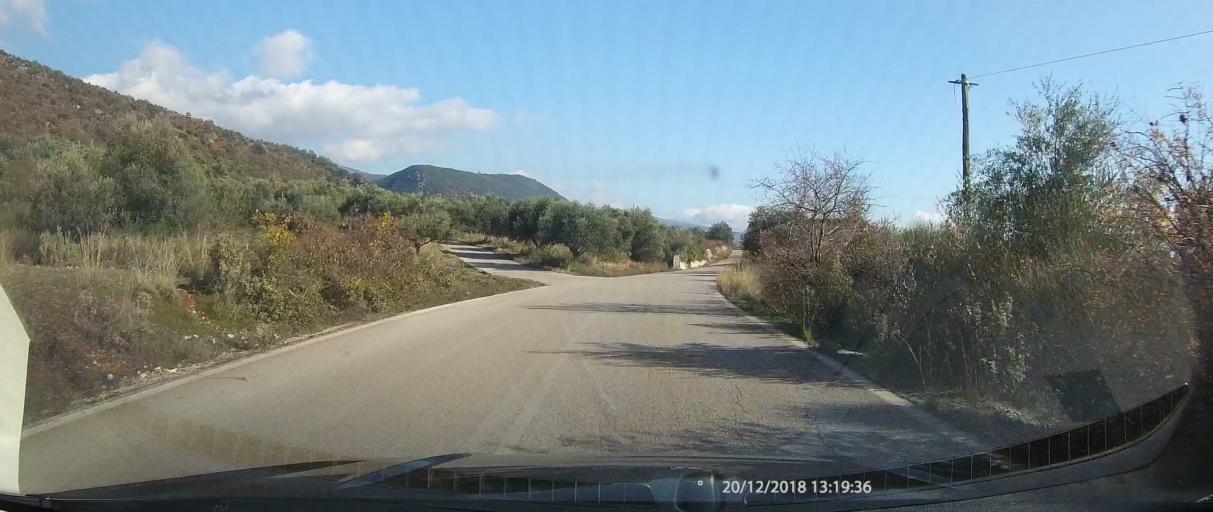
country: GR
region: West Greece
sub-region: Nomos Aitolias kai Akarnanias
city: Paravola
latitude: 38.6141
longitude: 21.5348
